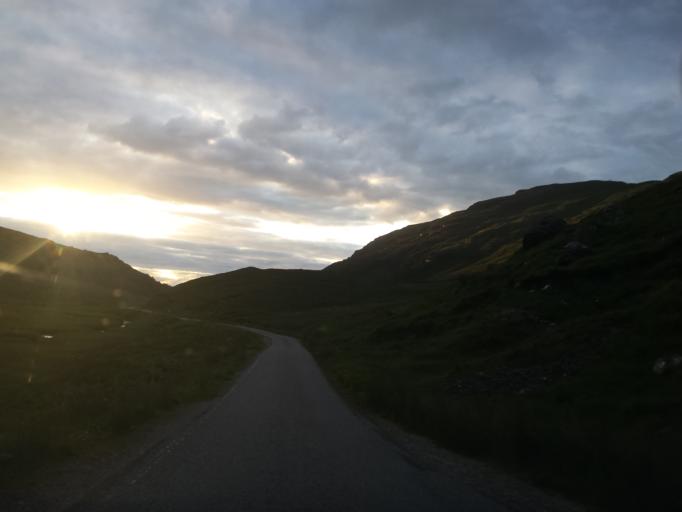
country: GB
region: Scotland
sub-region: Highland
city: Portree
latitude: 57.4878
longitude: -5.6072
